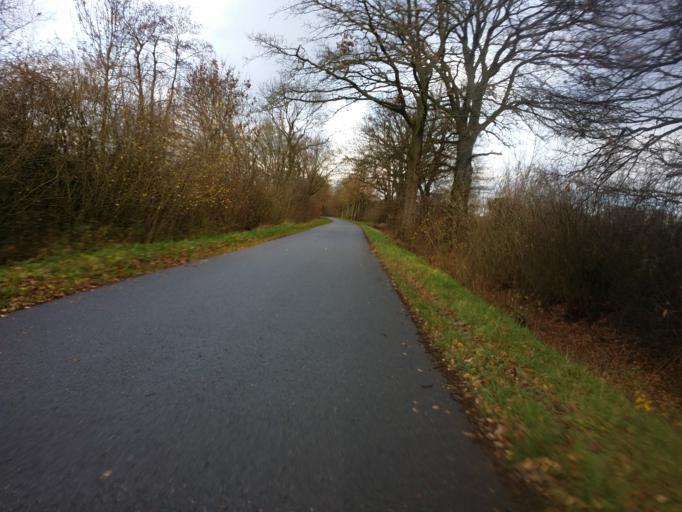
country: DE
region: Lower Saxony
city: Thedinghausen
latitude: 52.9725
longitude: 8.9897
